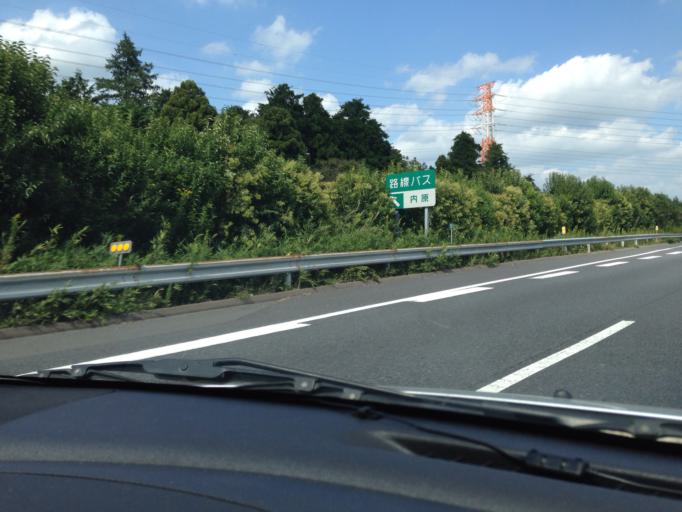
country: JP
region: Ibaraki
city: Tomobe
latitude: 36.3463
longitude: 140.3659
